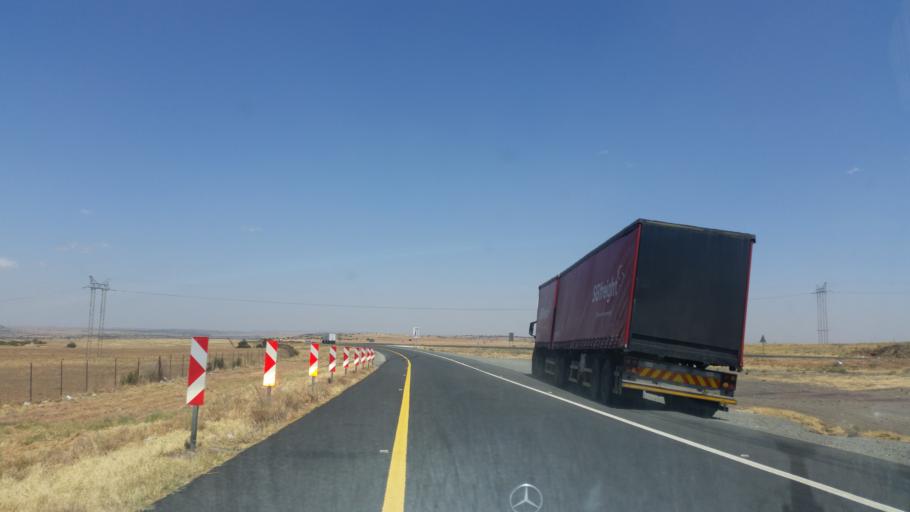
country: ZA
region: Orange Free State
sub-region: Lejweleputswa District Municipality
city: Winburg
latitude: -28.5012
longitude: 26.9970
